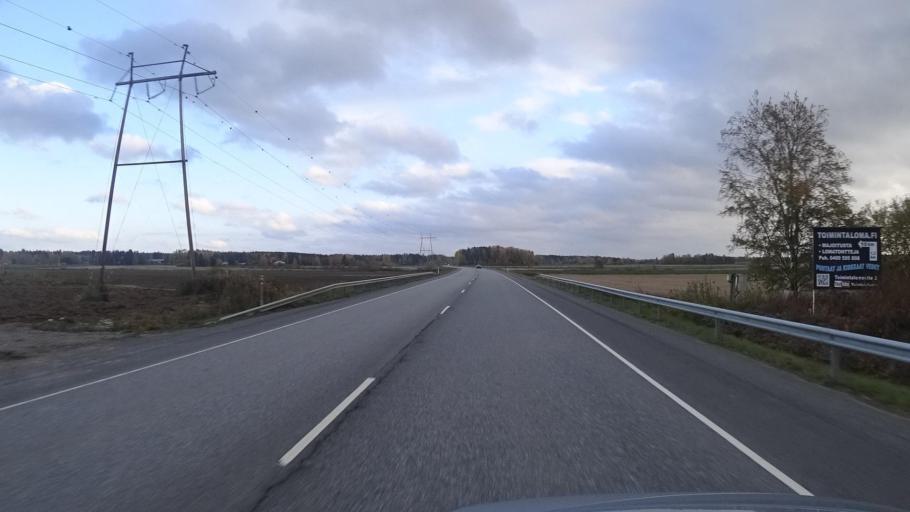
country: FI
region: Satakunta
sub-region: Rauma
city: Saekylae
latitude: 61.0308
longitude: 22.3944
